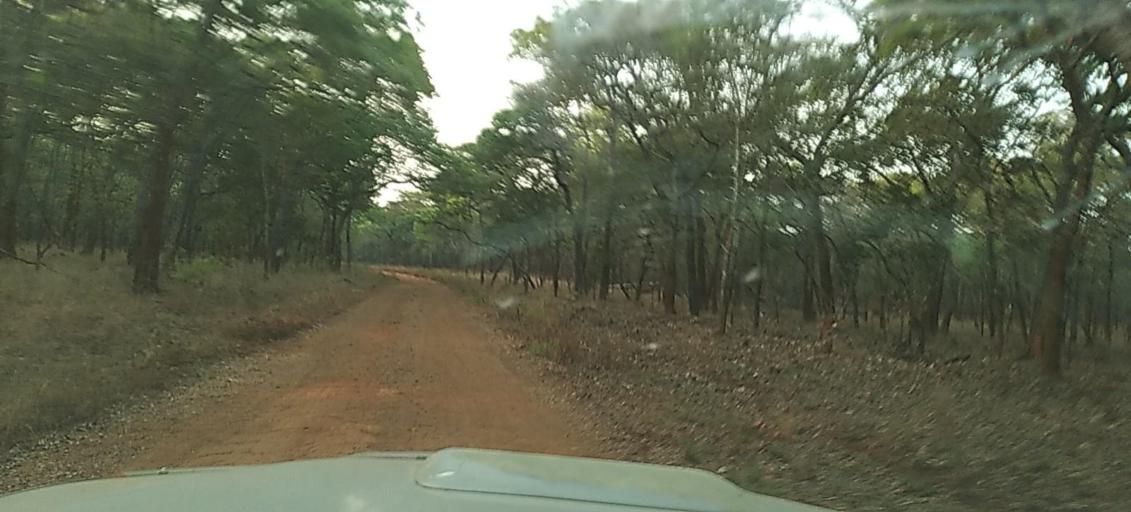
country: ZM
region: North-Western
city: Kasempa
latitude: -13.1038
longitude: 26.4050
